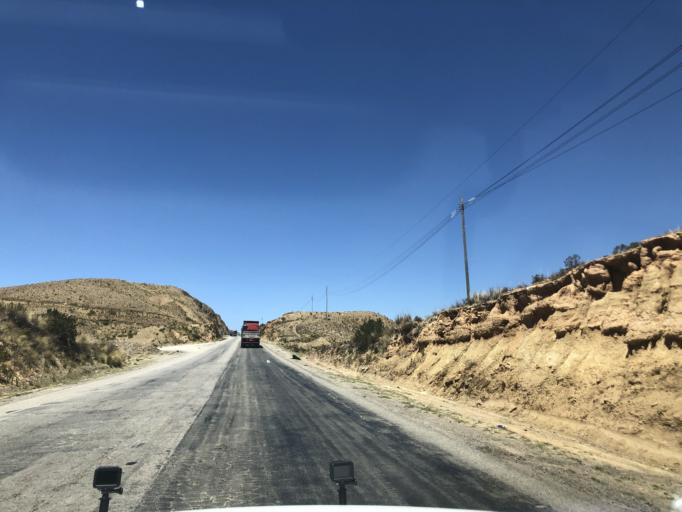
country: BO
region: Cochabamba
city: Sipe Sipe
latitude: -17.7112
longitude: -66.6358
